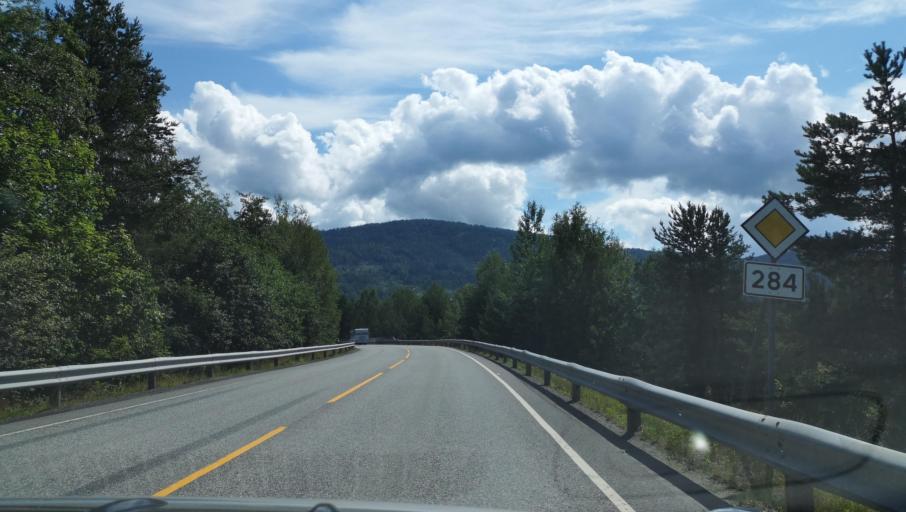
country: NO
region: Buskerud
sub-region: Modum
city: Vikersund
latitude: 59.9637
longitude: 9.9870
